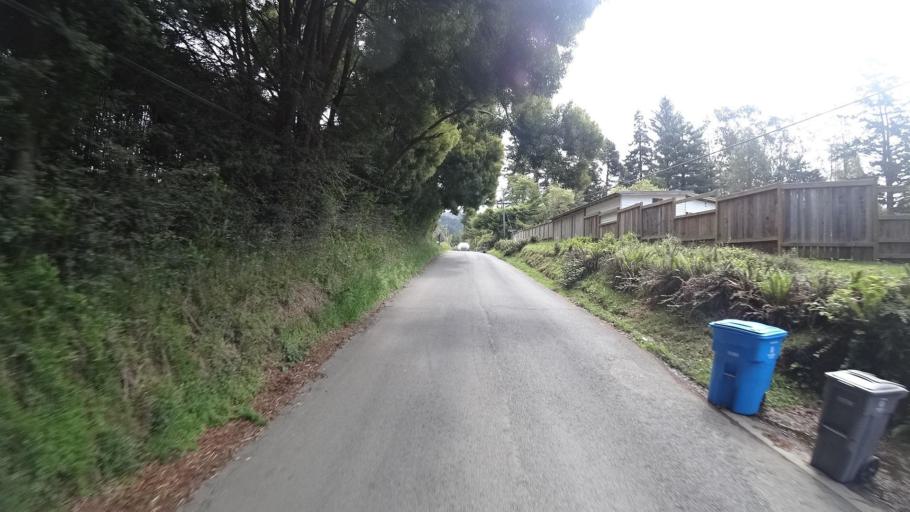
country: US
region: California
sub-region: Humboldt County
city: Bayside
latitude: 40.8491
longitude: -124.0620
